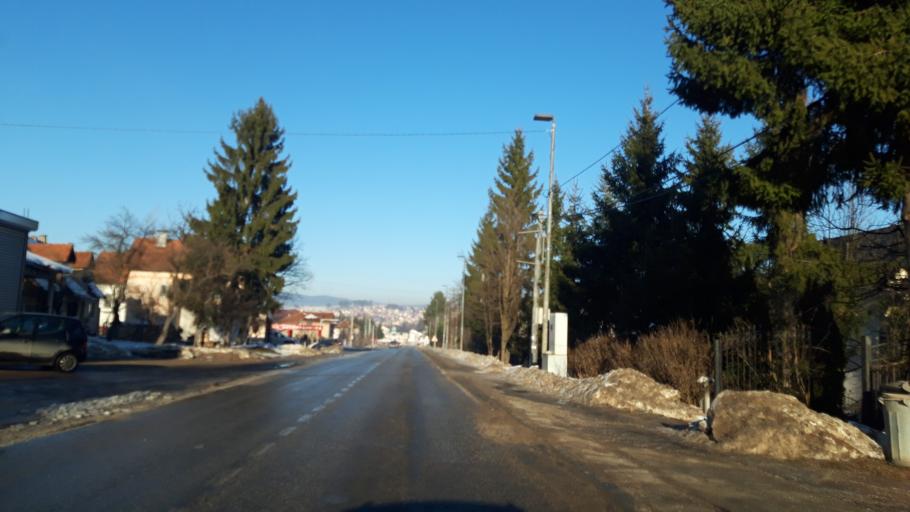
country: BA
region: Republika Srpska
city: Sokolac
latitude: 43.9299
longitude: 18.7886
